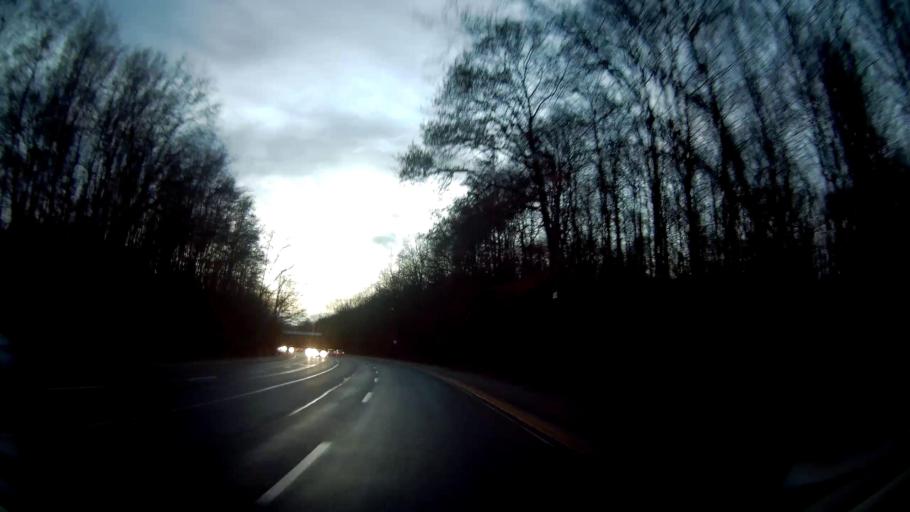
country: DE
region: North Rhine-Westphalia
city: Castrop-Rauxel
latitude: 51.4926
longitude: 7.2993
